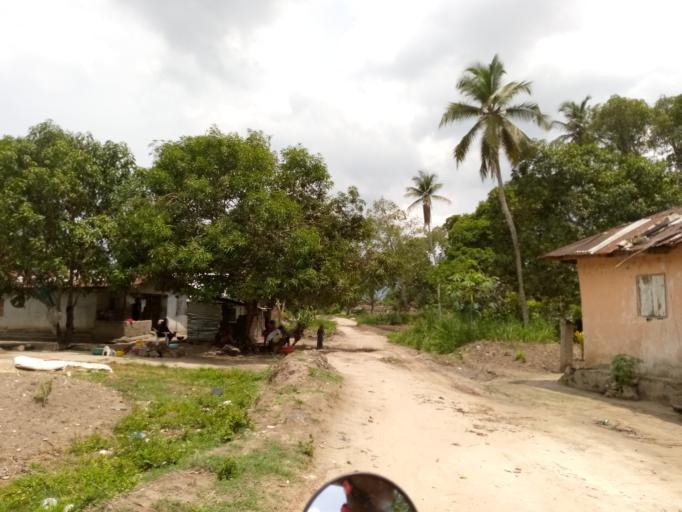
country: SL
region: Western Area
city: Waterloo
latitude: 8.3204
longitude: -13.0331
